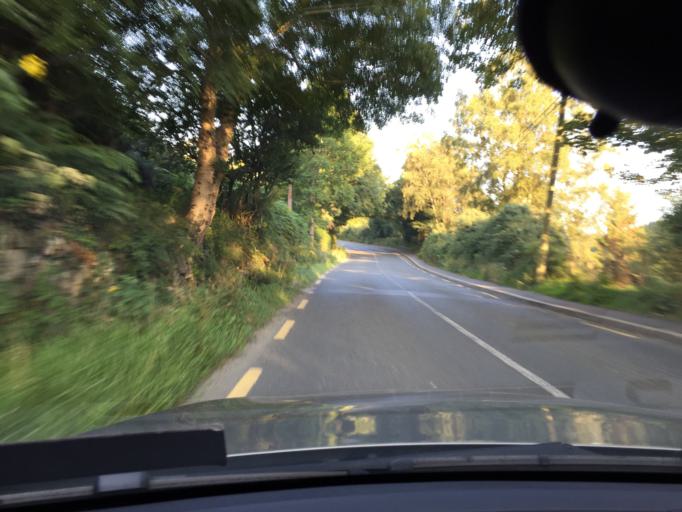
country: IE
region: Leinster
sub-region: Wicklow
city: Rathdrum
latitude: 53.0099
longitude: -6.3157
